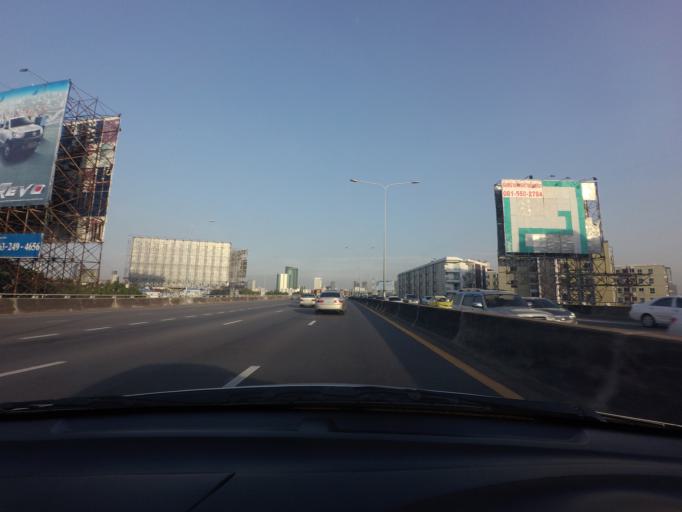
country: TH
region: Bangkok
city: Chatuchak
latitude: 13.8257
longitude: 100.5455
